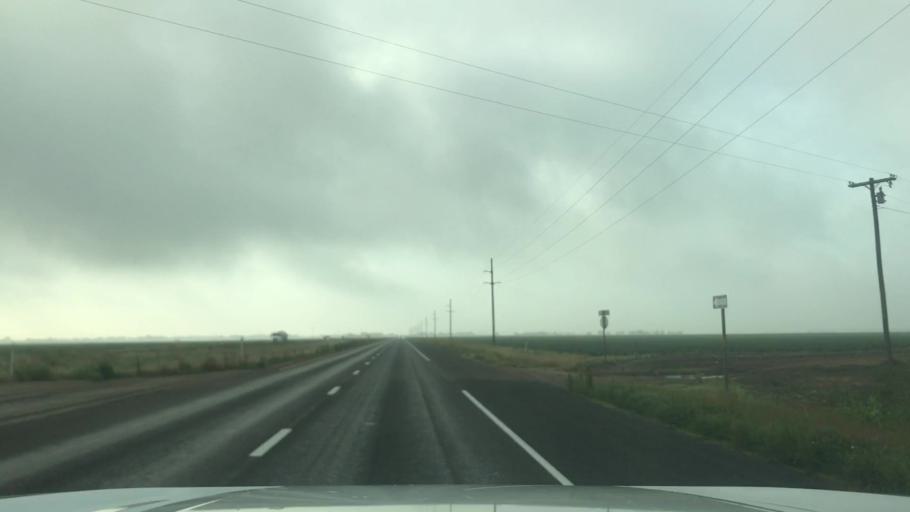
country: US
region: Texas
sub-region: Lubbock County
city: Slaton
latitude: 33.3718
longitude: -101.5734
